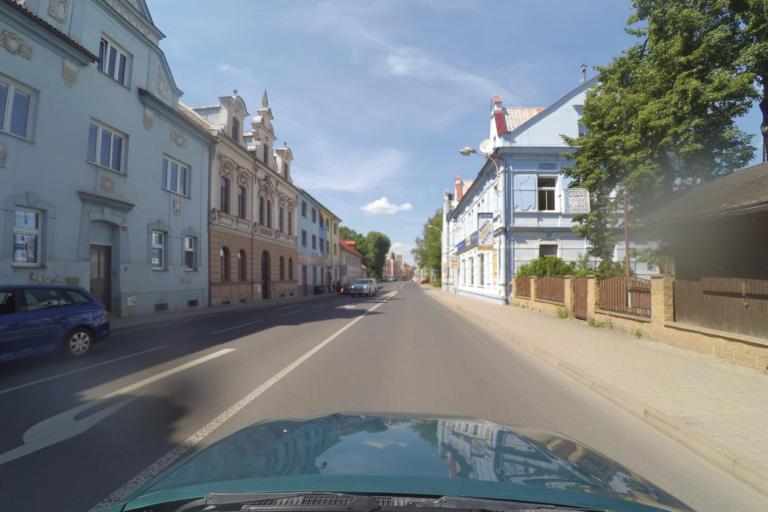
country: CZ
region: Liberecky
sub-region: Okres Ceska Lipa
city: Ceska Lipa
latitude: 50.6779
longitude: 14.5371
